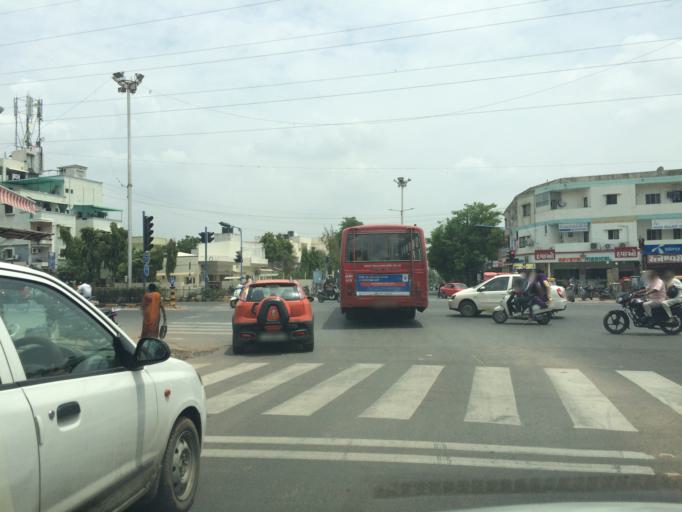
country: IN
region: Gujarat
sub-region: Ahmadabad
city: Ahmedabad
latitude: 23.0679
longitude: 72.5666
